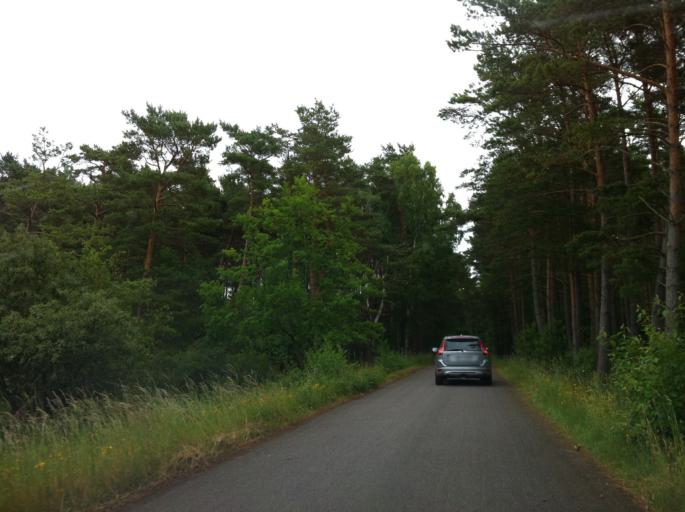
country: SE
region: Kalmar
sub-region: Vasterviks Kommun
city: Vaestervik
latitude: 57.3350
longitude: 17.0915
